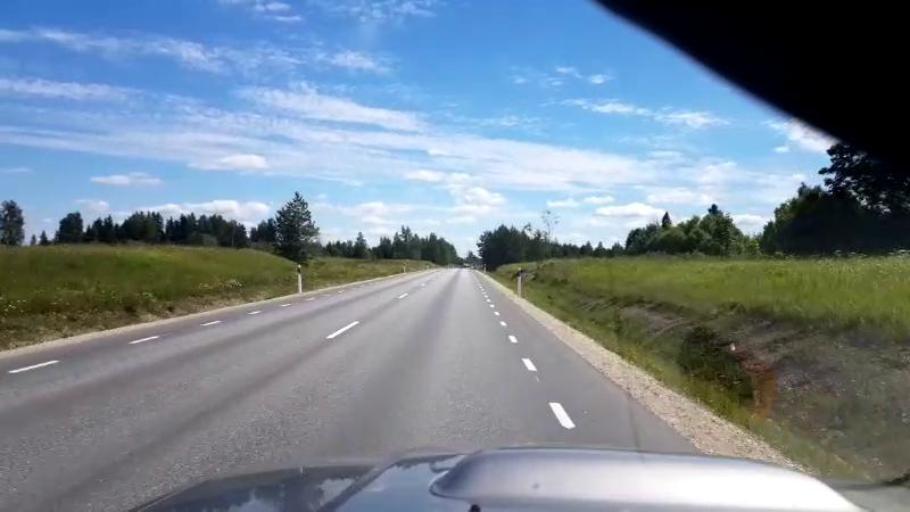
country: EE
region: Jogevamaa
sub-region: Jogeva linn
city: Jogeva
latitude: 58.7794
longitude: 26.3210
